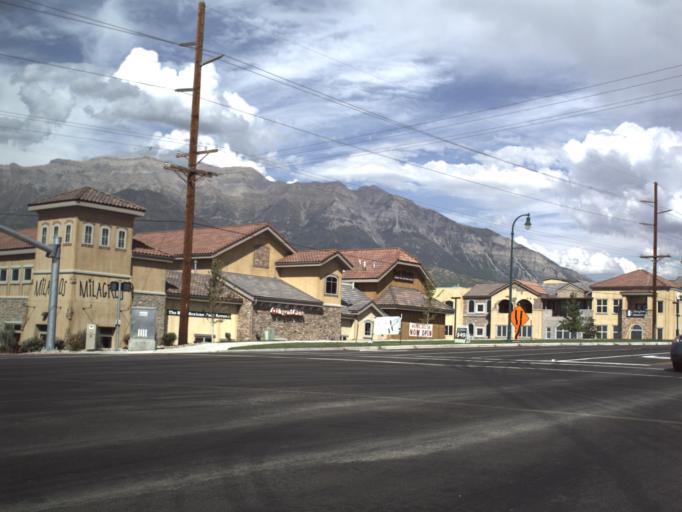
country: US
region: Utah
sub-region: Utah County
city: Lindon
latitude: 40.3118
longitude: -111.7227
